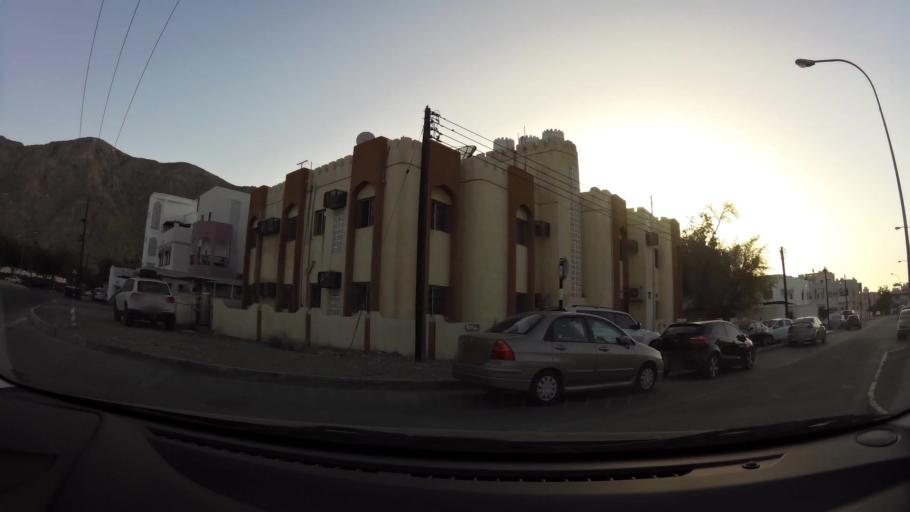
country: OM
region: Muhafazat Masqat
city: Muscat
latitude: 23.5730
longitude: 58.5697
